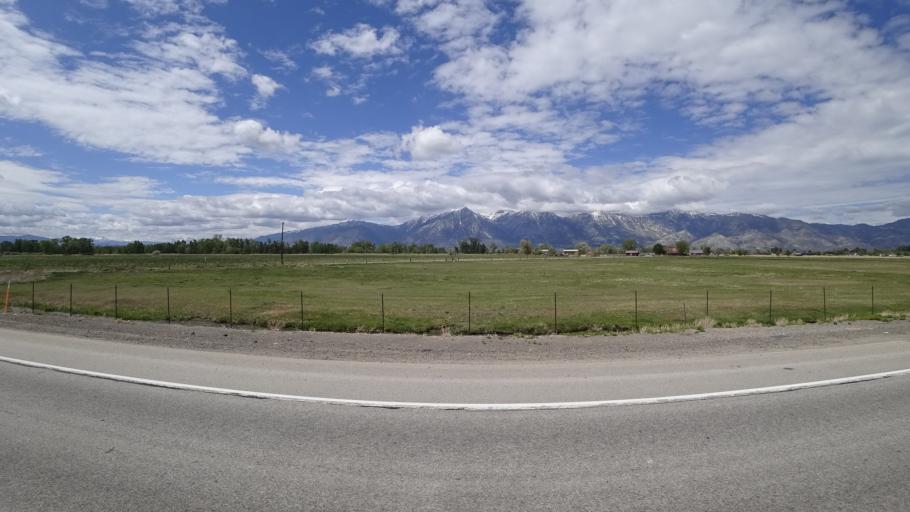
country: US
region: Nevada
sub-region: Douglas County
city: Gardnerville
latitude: 38.9293
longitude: -119.7312
